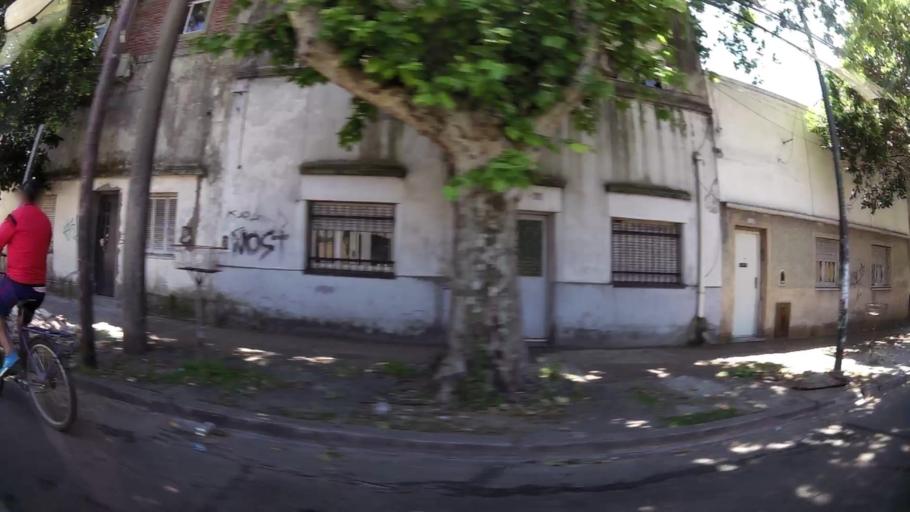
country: AR
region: Buenos Aires
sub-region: Partido de General San Martin
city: General San Martin
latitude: -34.5749
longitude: -58.5279
